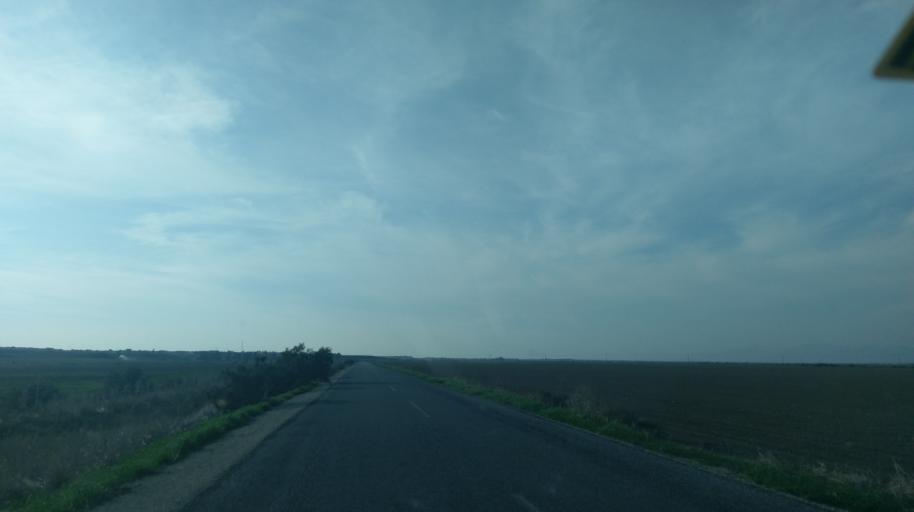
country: CY
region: Ammochostos
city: Acheritou
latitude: 35.0954
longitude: 33.8267
